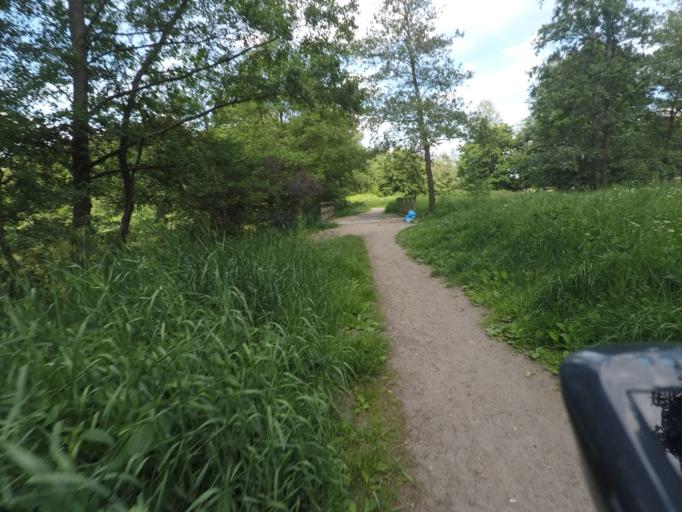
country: DE
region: Schleswig-Holstein
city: Barsbuettel
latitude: 53.6110
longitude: 10.1705
